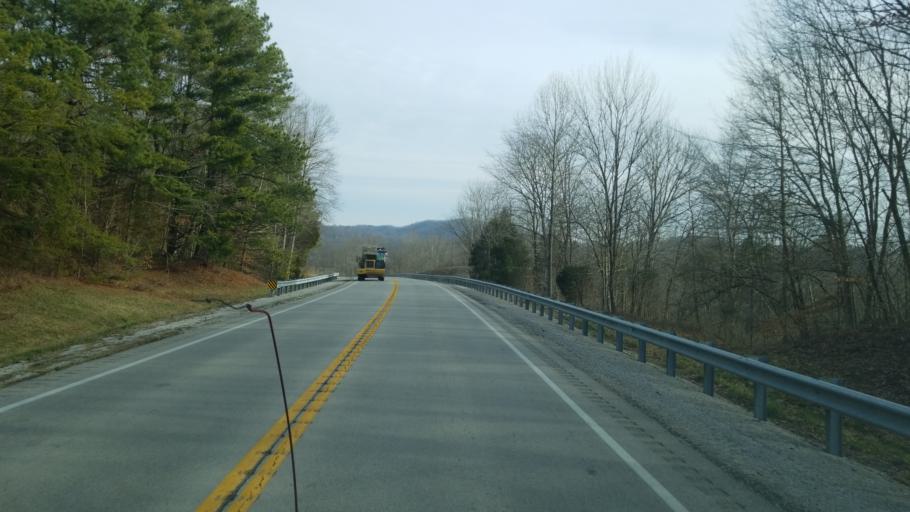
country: US
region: Kentucky
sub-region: Casey County
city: Liberty
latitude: 37.3533
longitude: -84.8704
